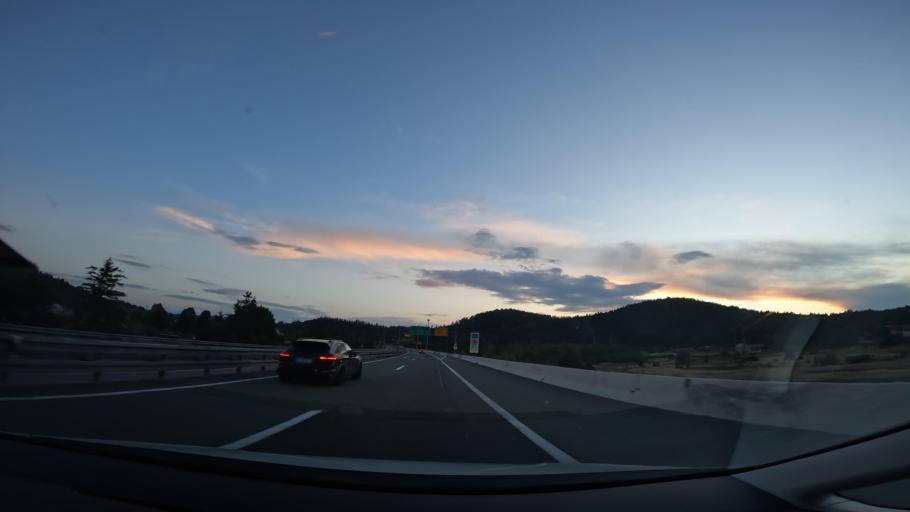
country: HR
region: Primorsko-Goranska
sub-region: Grad Delnice
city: Delnice
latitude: 45.3213
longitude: 14.7304
